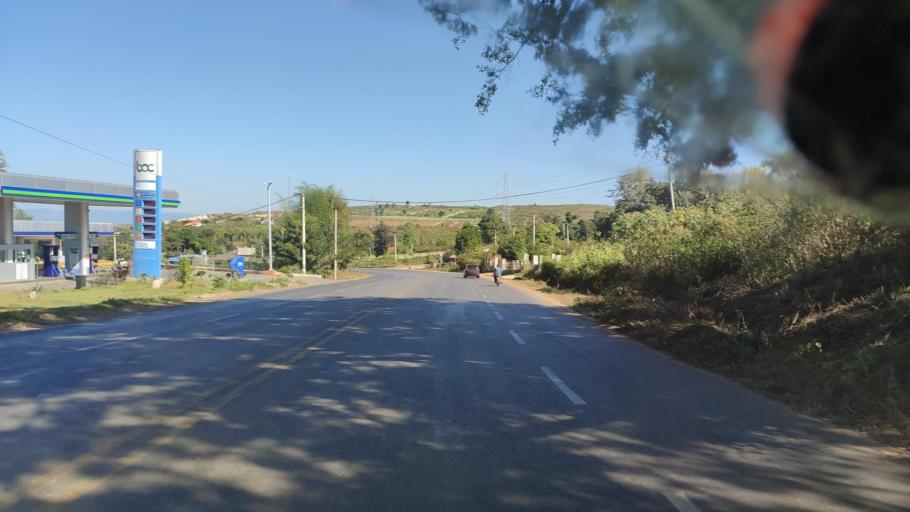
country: MM
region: Mandalay
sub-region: Pyin Oo Lwin District
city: Pyin Oo Lwin
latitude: 22.0677
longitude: 96.5748
